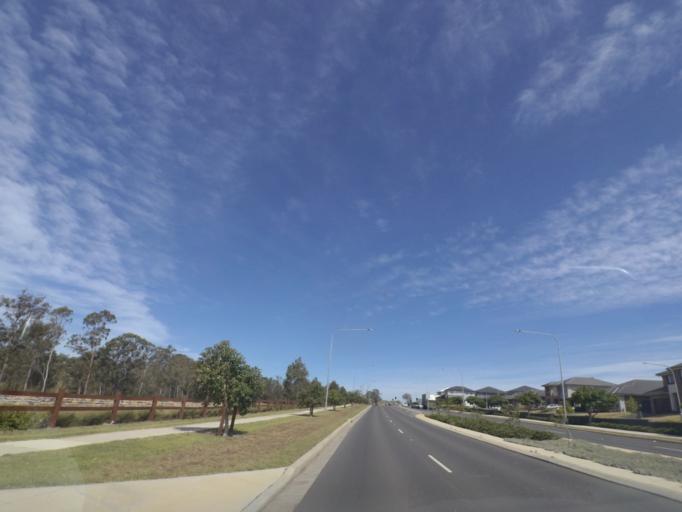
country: AU
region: New South Wales
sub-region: Camden
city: Narellan Vale
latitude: -34.0264
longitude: 150.7846
